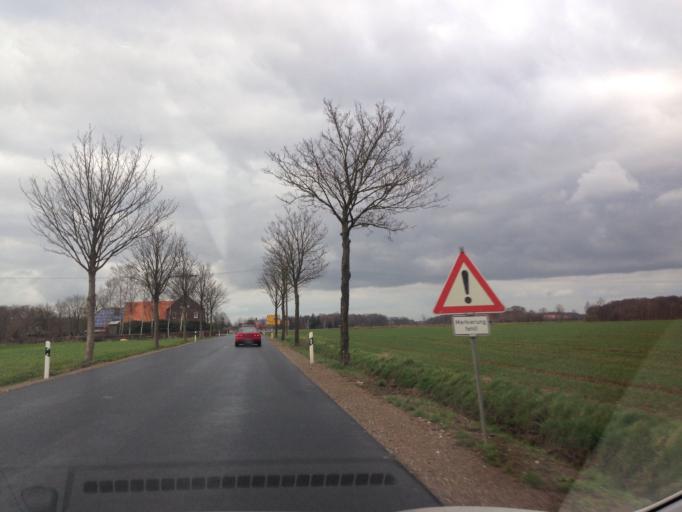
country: DE
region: North Rhine-Westphalia
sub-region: Regierungsbezirk Munster
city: Nordkirchen
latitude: 51.7841
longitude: 7.5427
